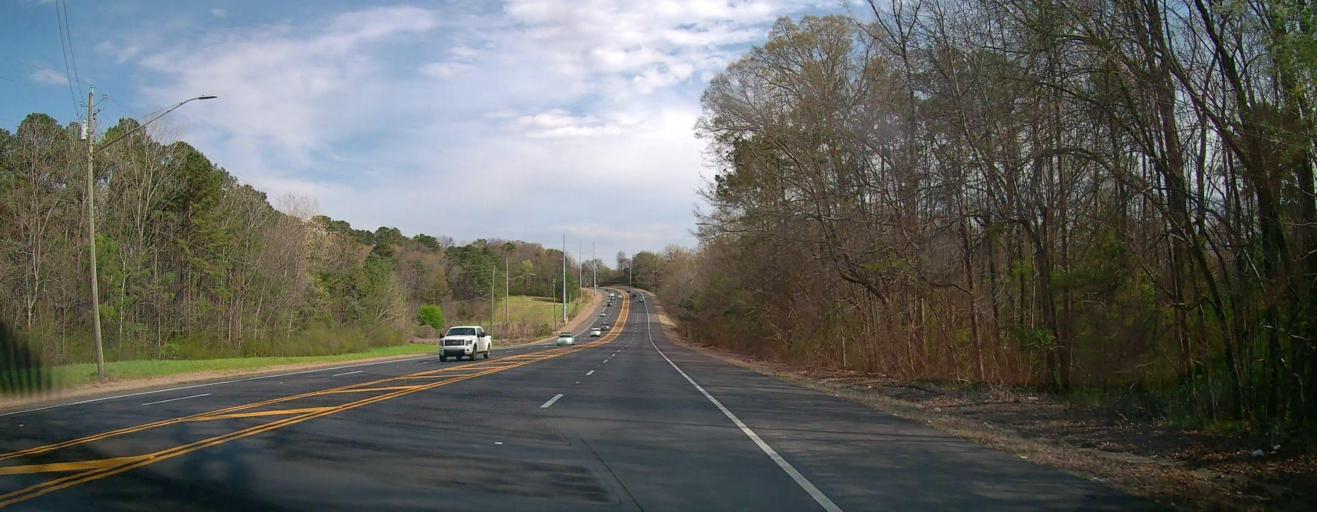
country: US
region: Alabama
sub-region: Jefferson County
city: Forestdale
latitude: 33.5386
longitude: -86.8688
